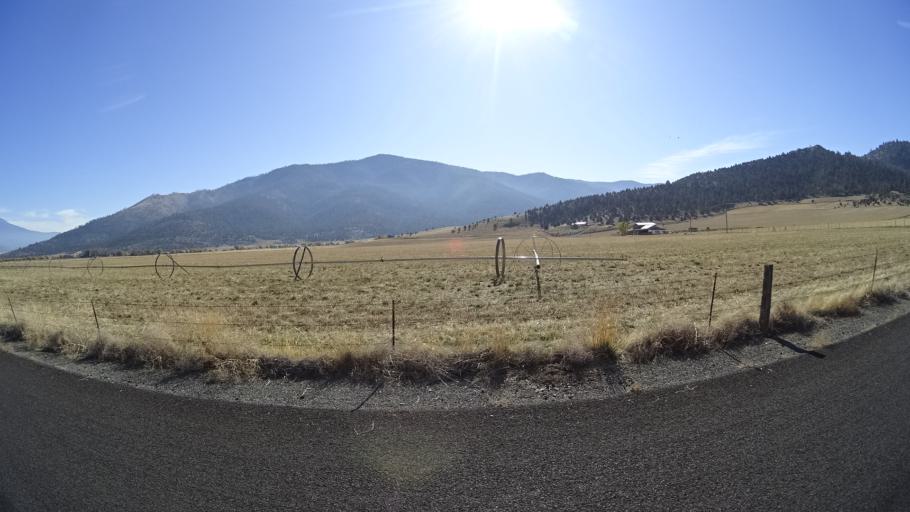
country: US
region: California
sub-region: Siskiyou County
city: Weed
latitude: 41.5033
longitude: -122.5539
